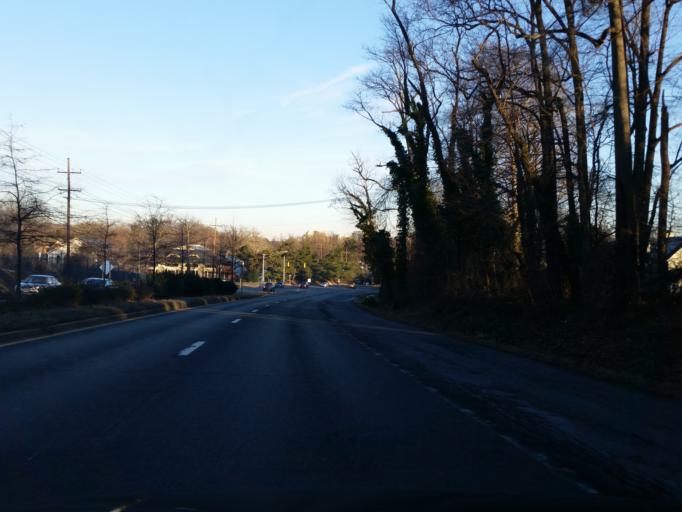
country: US
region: Maryland
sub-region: Montgomery County
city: Bethesda
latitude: 38.9702
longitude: -77.1142
